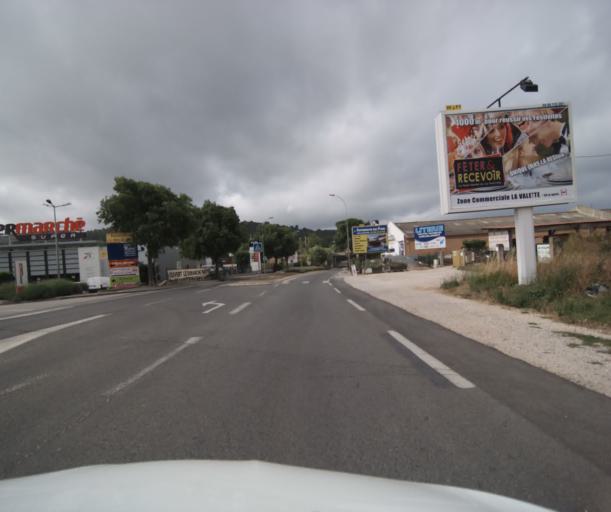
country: FR
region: Provence-Alpes-Cote d'Azur
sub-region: Departement du Var
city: Sanary-sur-Mer
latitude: 43.1242
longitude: 5.8229
